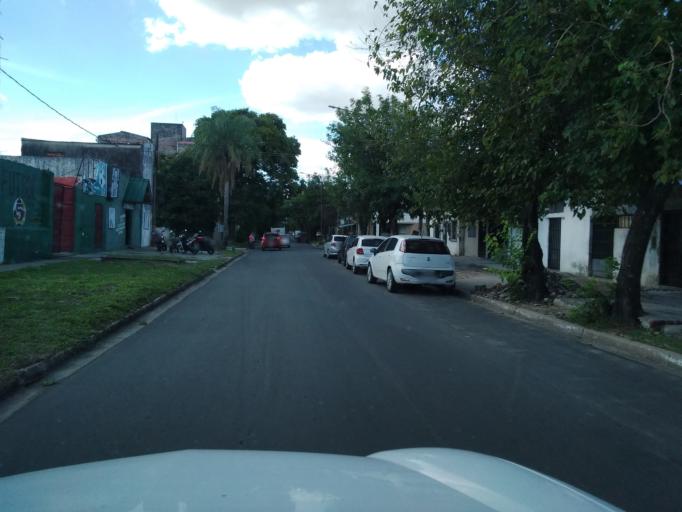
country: AR
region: Corrientes
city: Corrientes
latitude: -27.4846
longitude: -58.8376
